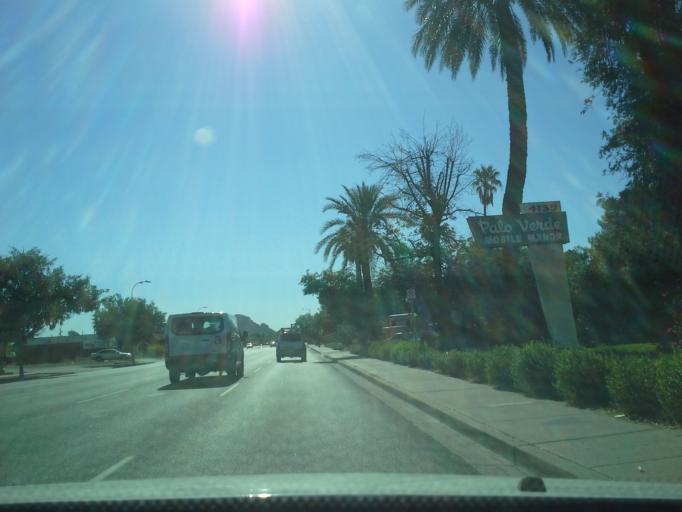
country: US
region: Arizona
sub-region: Maricopa County
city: Tempe Junction
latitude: 33.4656
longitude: -111.9918
